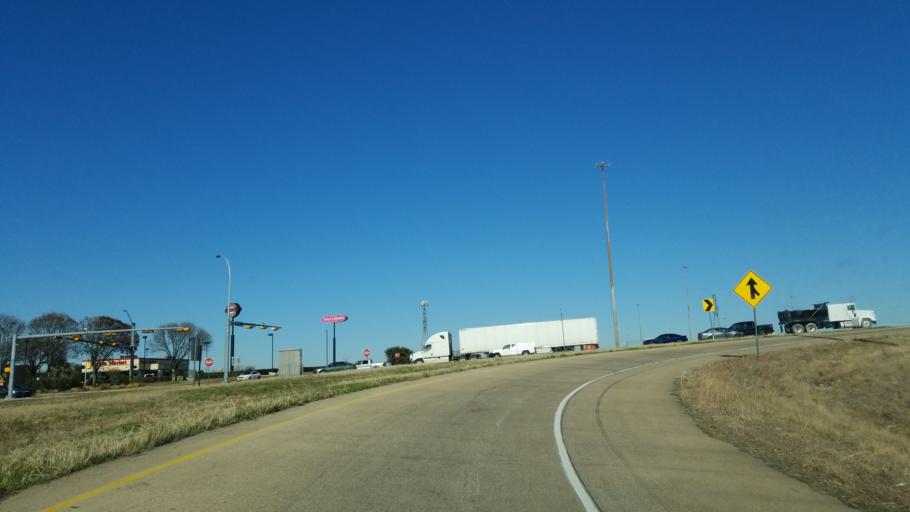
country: US
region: Texas
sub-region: Tarrant County
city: Arlington
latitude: 32.7115
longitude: -97.0644
